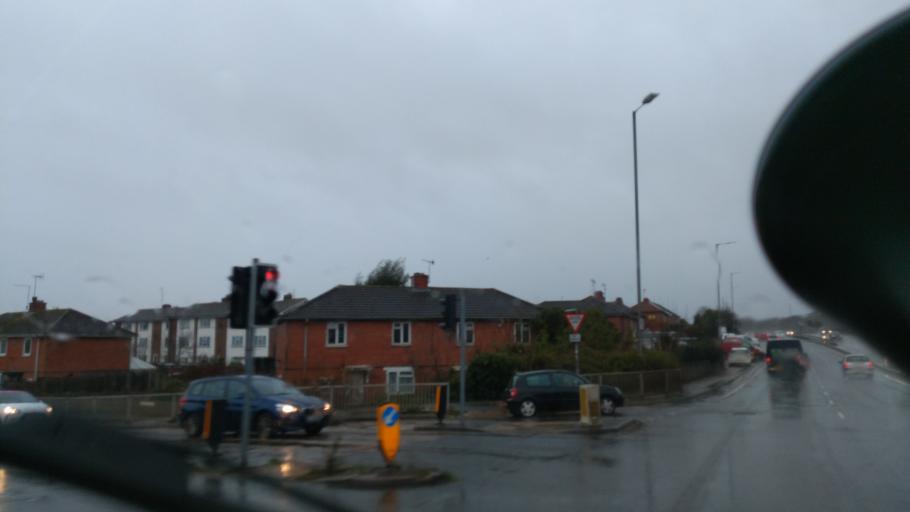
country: GB
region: England
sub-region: West Sussex
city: Lancing
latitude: 50.8376
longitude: -0.3361
